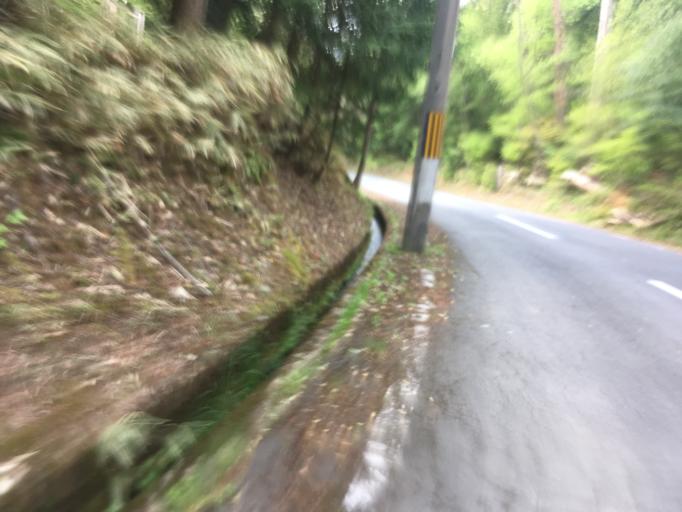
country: JP
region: Kyoto
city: Kameoka
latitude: 35.0906
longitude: 135.6087
